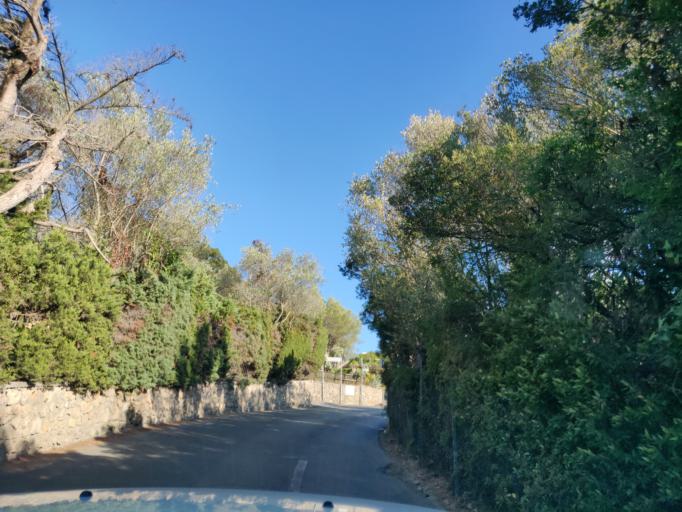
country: IT
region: Tuscany
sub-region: Provincia di Grosseto
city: Orbetello Scalo
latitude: 42.4176
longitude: 11.2824
